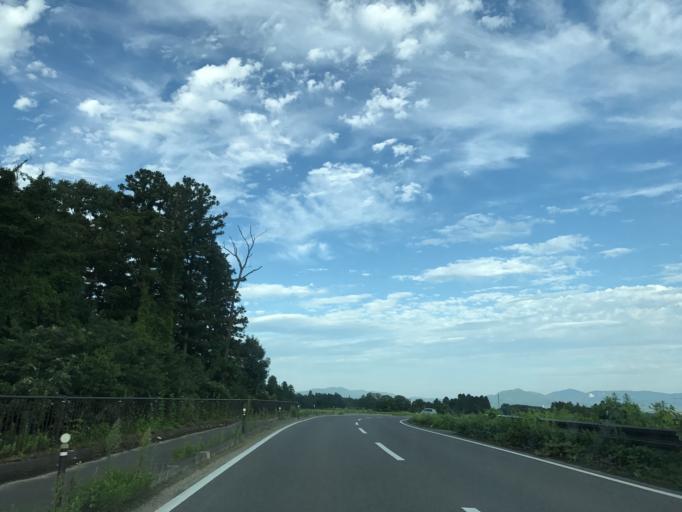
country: JP
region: Fukushima
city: Sukagawa
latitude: 37.3292
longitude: 140.3470
